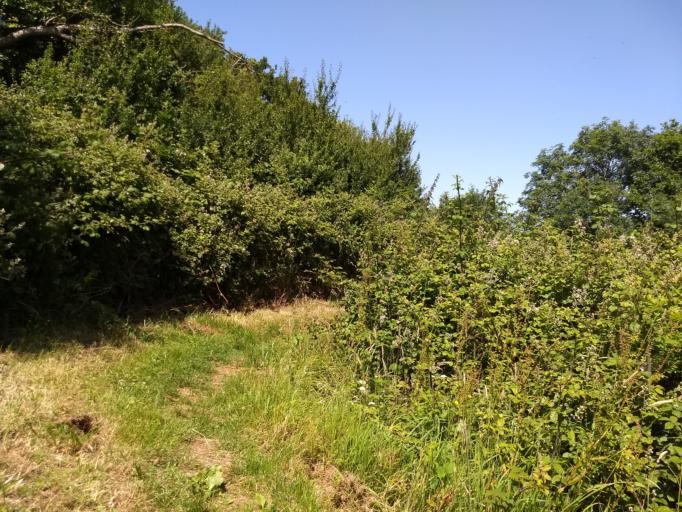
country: GB
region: England
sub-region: Isle of Wight
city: Shalfleet
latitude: 50.6890
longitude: -1.4161
